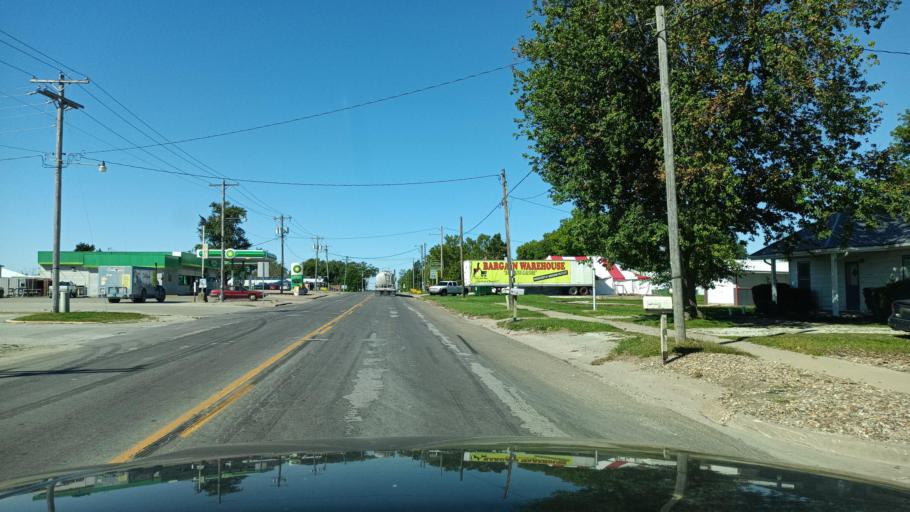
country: US
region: Missouri
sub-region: Scotland County
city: Memphis
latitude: 40.4514
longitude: -92.1639
